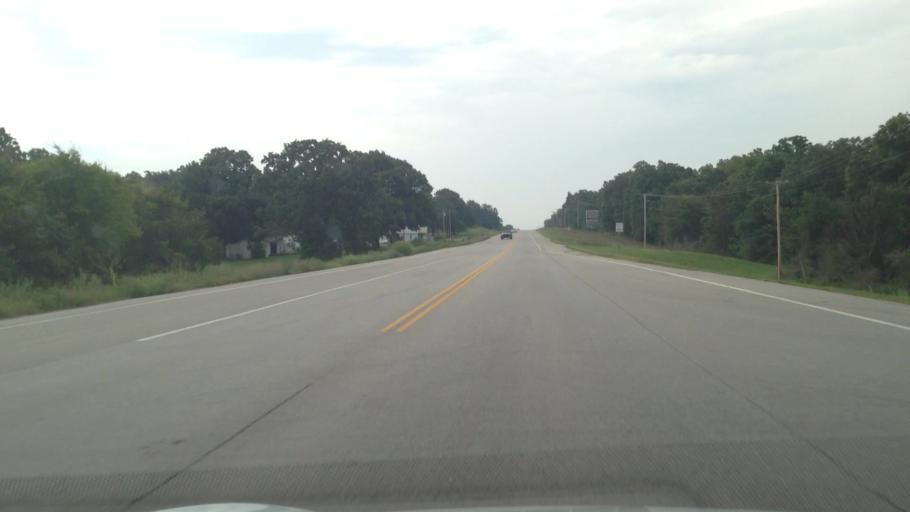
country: US
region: Kansas
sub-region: Cherokee County
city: Galena
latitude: 37.0236
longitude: -94.6675
